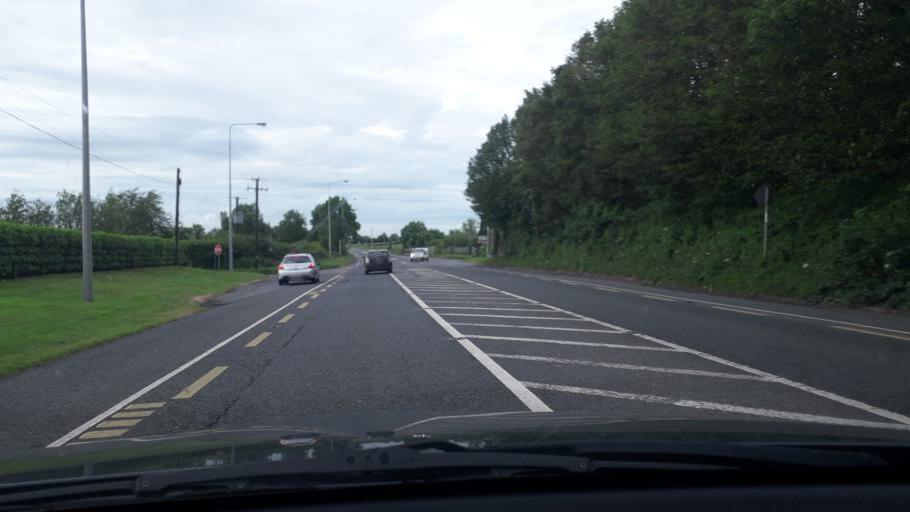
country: IE
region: Leinster
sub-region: County Carlow
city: Carlow
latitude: 52.7824
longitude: -6.9503
